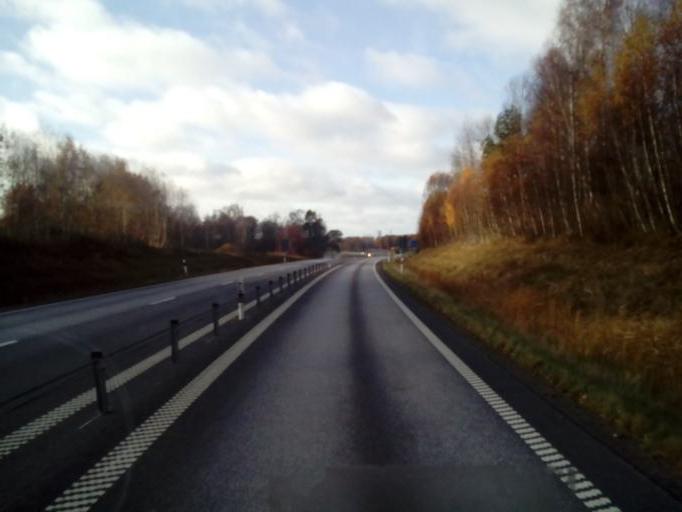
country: SE
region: Kalmar
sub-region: Vimmerby Kommun
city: Vimmerby
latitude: 57.6622
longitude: 15.8867
